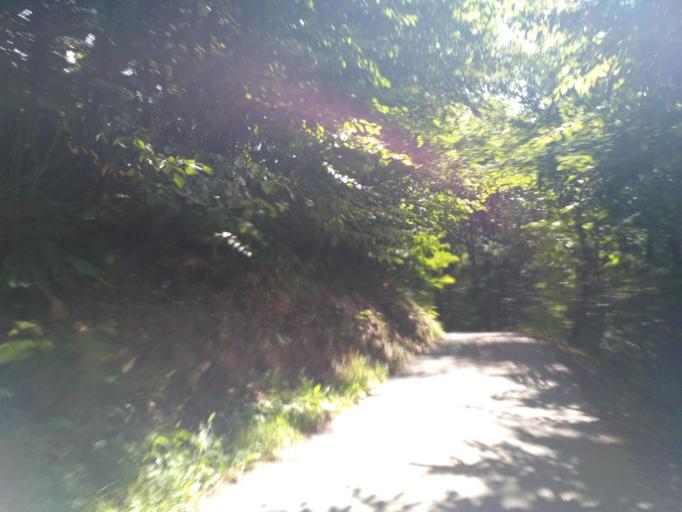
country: PL
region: Subcarpathian Voivodeship
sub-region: Powiat strzyzowski
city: Polomia
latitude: 49.9158
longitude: 21.8851
